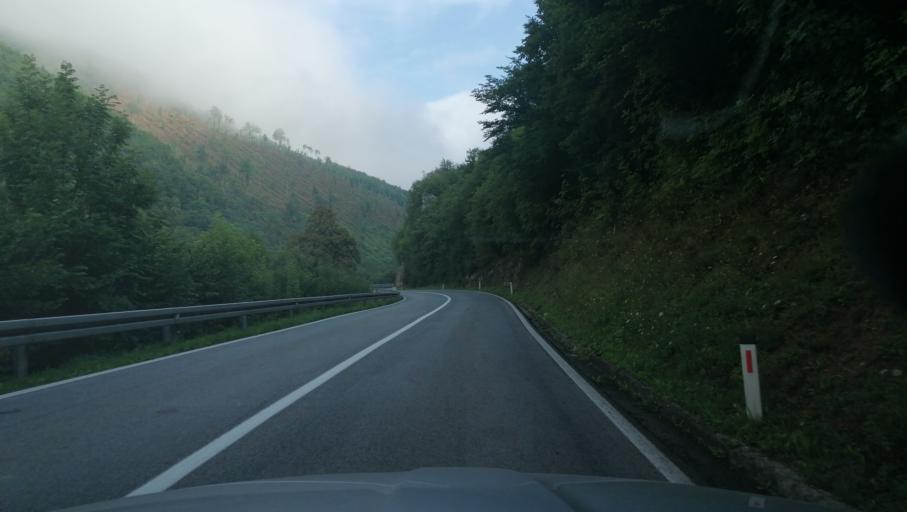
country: BA
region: Federation of Bosnia and Herzegovina
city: Donji Vakuf
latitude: 44.1857
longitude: 17.3435
